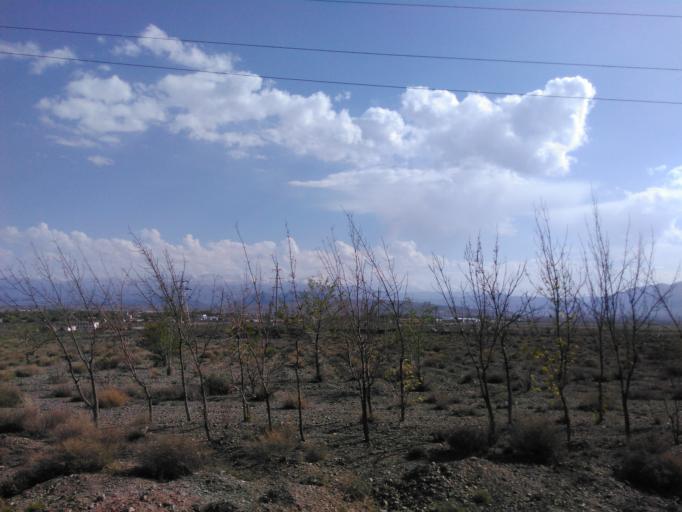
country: KG
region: Ysyk-Koel
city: Balykchy
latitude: 42.4552
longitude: 76.1521
